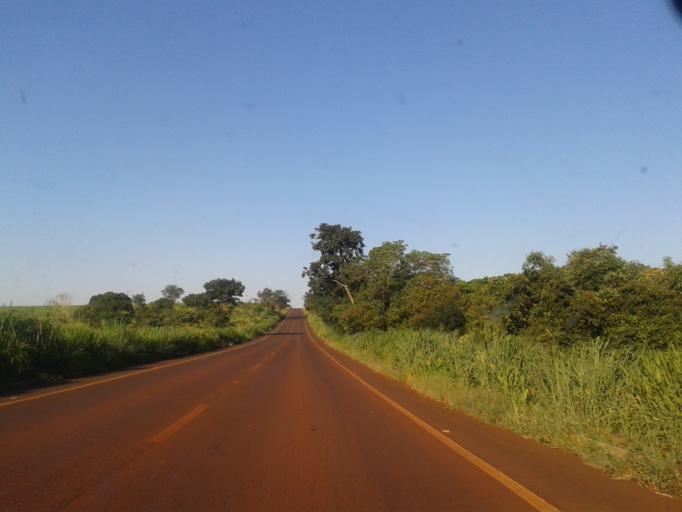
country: BR
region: Minas Gerais
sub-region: Capinopolis
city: Capinopolis
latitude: -18.7079
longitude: -49.7033
